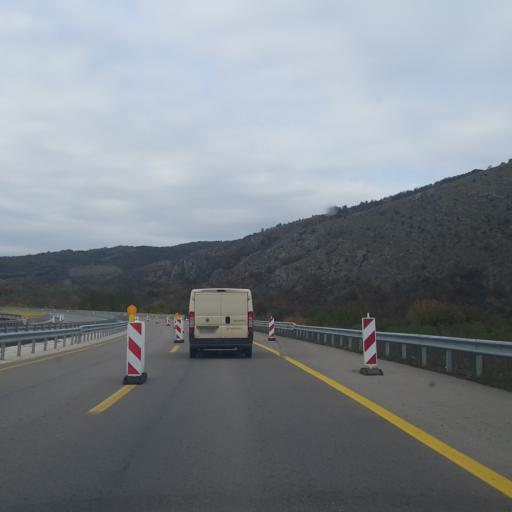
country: RS
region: Central Serbia
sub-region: Pirotski Okrug
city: Bela Palanka
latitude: 43.2331
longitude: 22.3779
